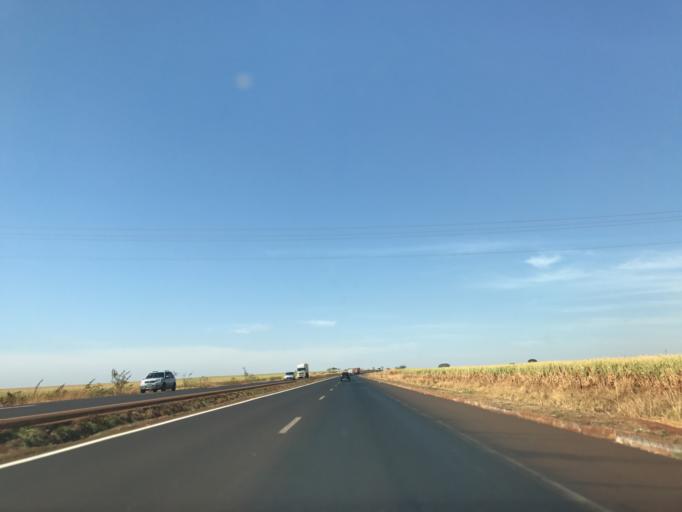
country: BR
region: Minas Gerais
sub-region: Centralina
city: Centralina
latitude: -18.5096
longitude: -49.1892
